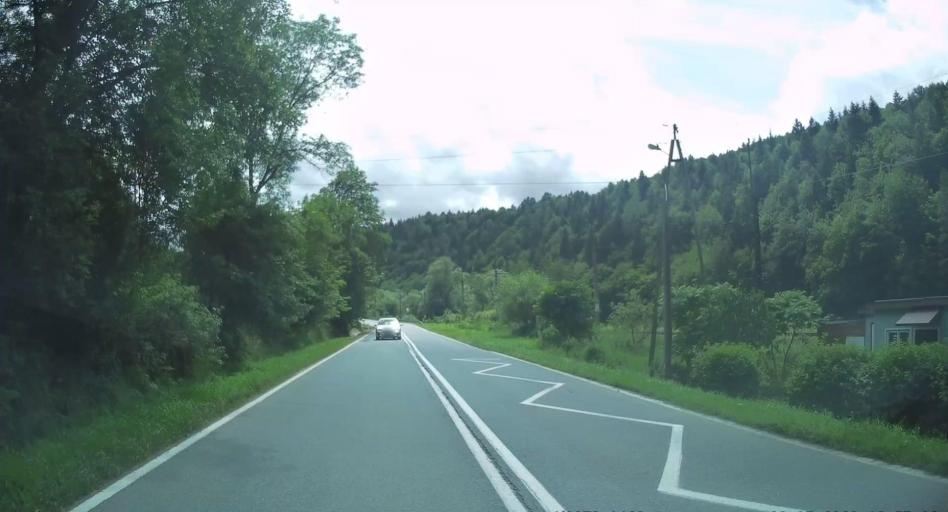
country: PL
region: Lesser Poland Voivodeship
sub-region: Powiat nowosadecki
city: Piwniczna-Zdroj
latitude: 49.3774
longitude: 20.7595
